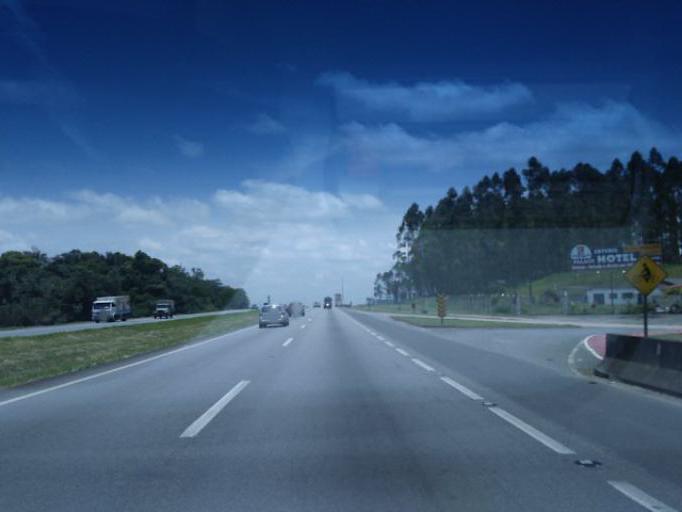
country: BR
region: Sao Paulo
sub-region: Registro
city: Registro
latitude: -24.4705
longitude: -47.8237
